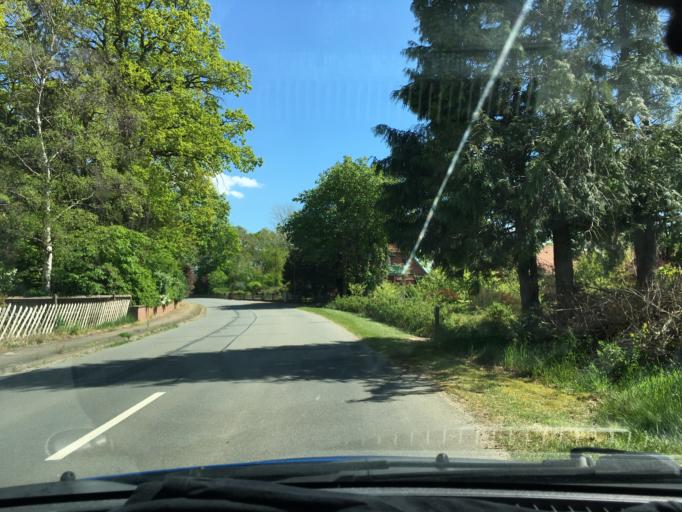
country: DE
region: Lower Saxony
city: Himbergen
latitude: 53.0862
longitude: 10.7406
